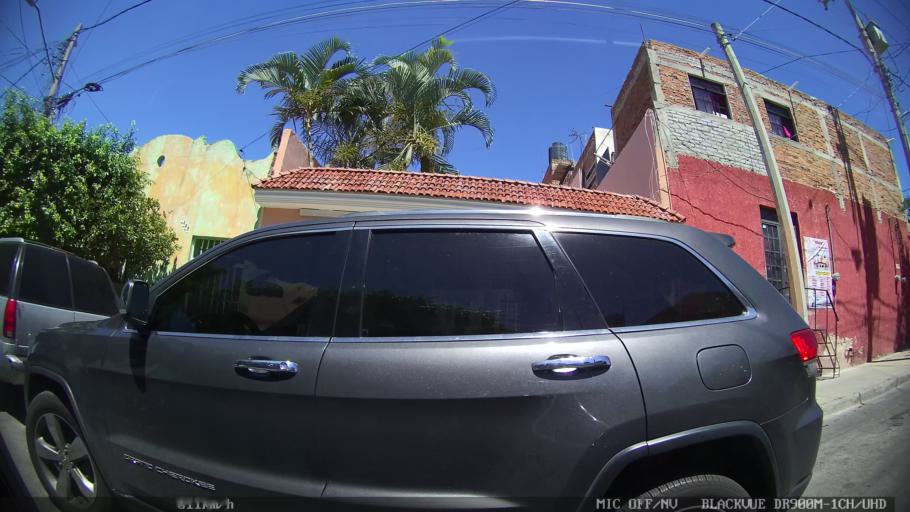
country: MX
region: Jalisco
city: Tlaquepaque
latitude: 20.6948
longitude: -103.2929
